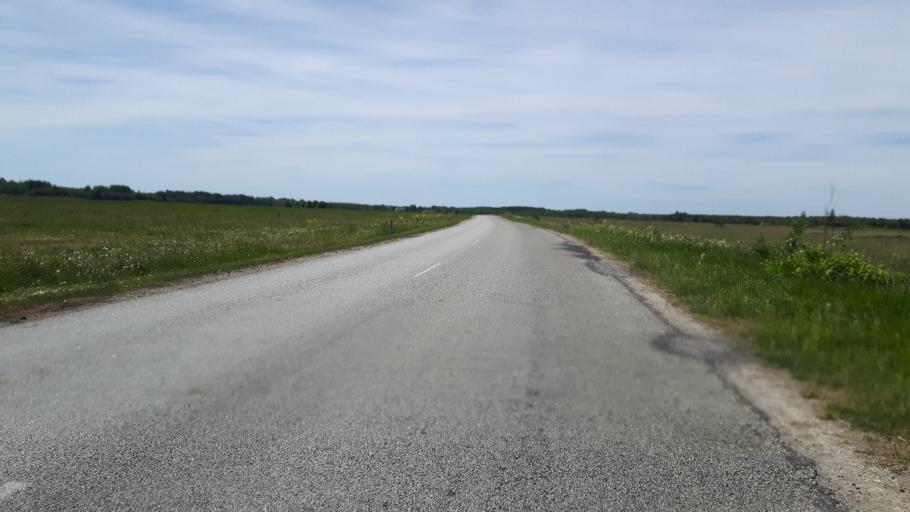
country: EE
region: Harju
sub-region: Kuusalu vald
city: Kuusalu
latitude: 59.4608
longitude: 25.3395
